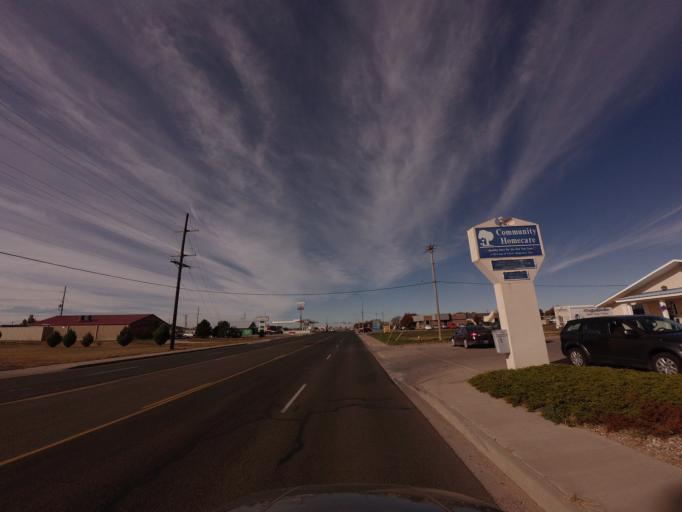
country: US
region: New Mexico
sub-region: Curry County
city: Clovis
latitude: 34.4194
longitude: -103.2292
